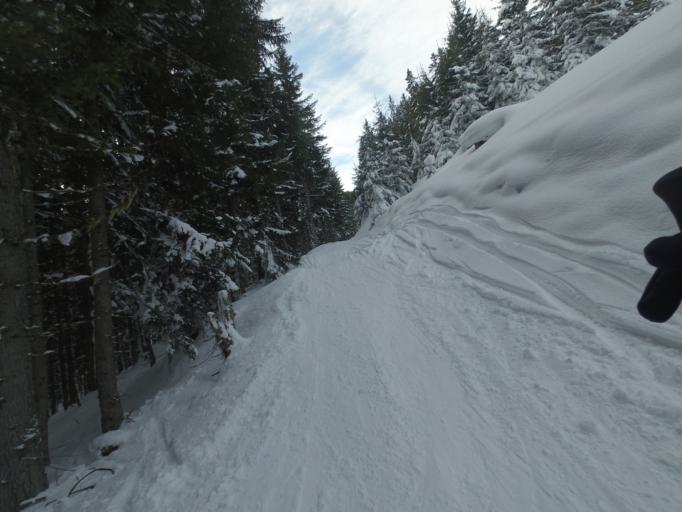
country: AT
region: Salzburg
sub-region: Politischer Bezirk Zell am See
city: Lend
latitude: 47.2762
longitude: 13.0134
